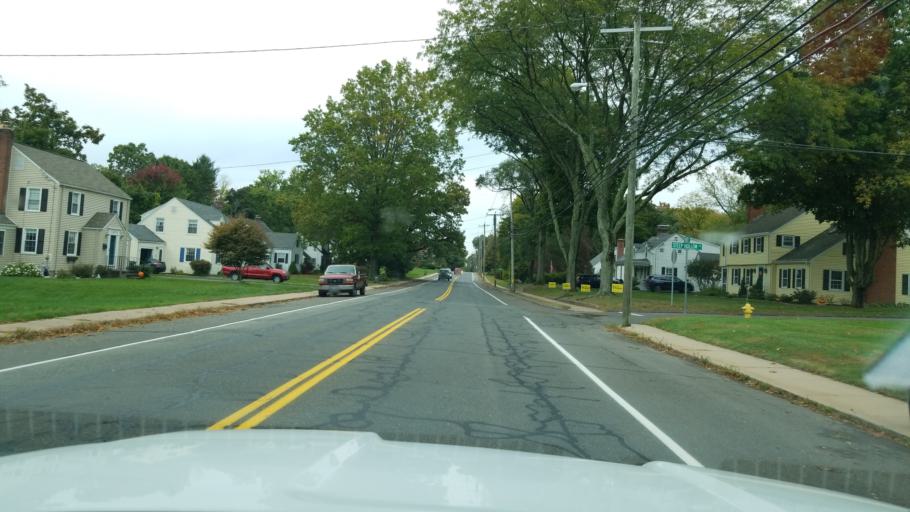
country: US
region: Connecticut
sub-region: Hartford County
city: Manchester
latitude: 41.7731
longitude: -72.4968
